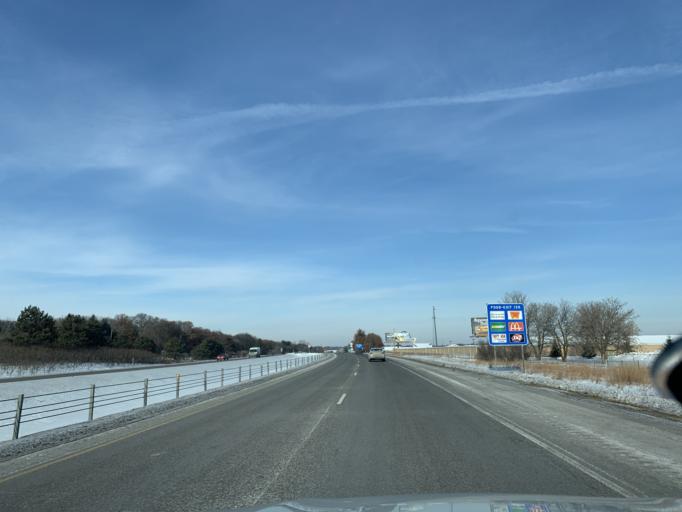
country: US
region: Minnesota
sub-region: Chisago County
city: Wyoming
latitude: 45.3243
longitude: -93.0032
